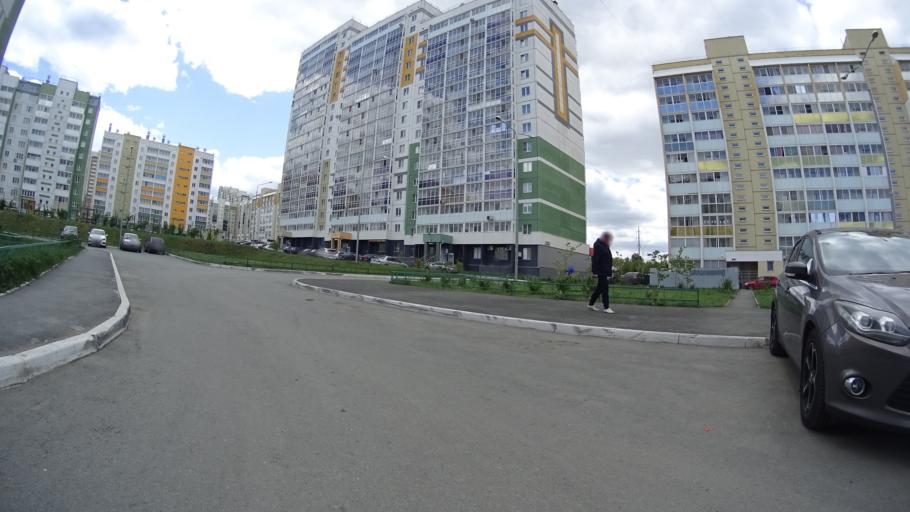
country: RU
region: Chelyabinsk
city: Roshchino
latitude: 55.1751
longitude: 61.2586
